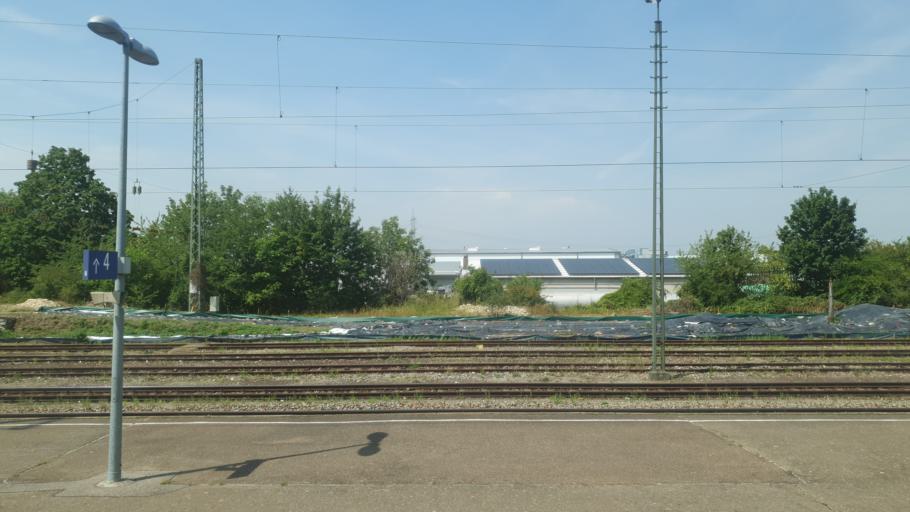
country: DE
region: Baden-Wuerttemberg
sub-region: Freiburg Region
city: Auggen
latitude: 47.8082
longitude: 7.5984
